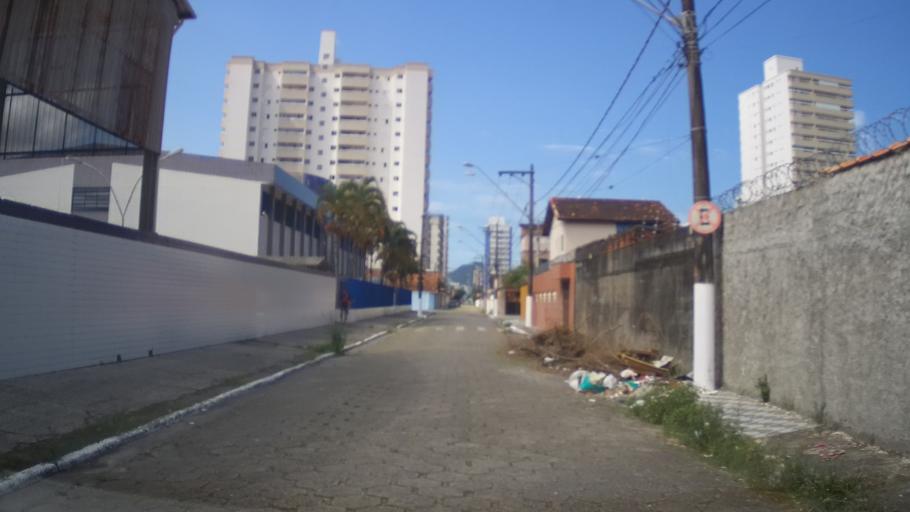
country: BR
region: Sao Paulo
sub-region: Praia Grande
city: Praia Grande
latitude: -24.0177
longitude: -46.4522
